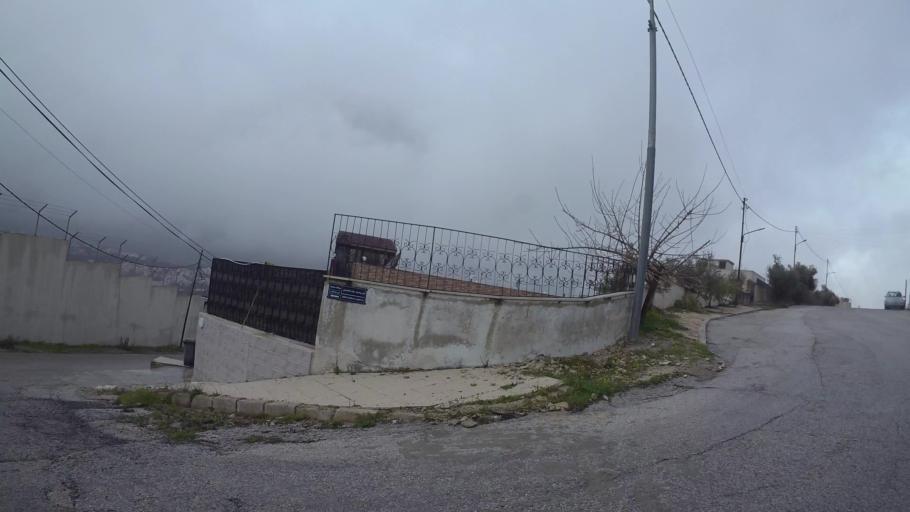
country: JO
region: Amman
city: Al Jubayhah
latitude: 32.0238
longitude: 35.8269
